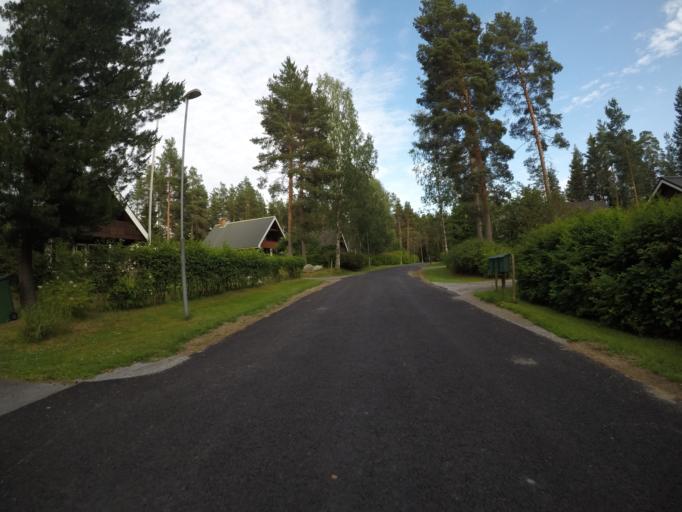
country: FI
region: Haeme
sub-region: Haemeenlinna
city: Haemeenlinna
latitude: 60.9707
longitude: 24.3918
